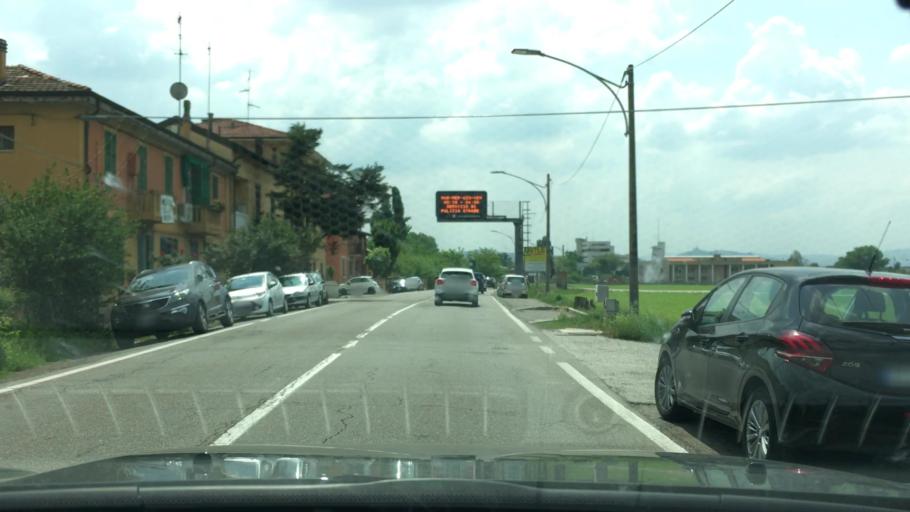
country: IT
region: Emilia-Romagna
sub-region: Provincia di Bologna
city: Progresso
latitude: 44.5402
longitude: 11.3714
